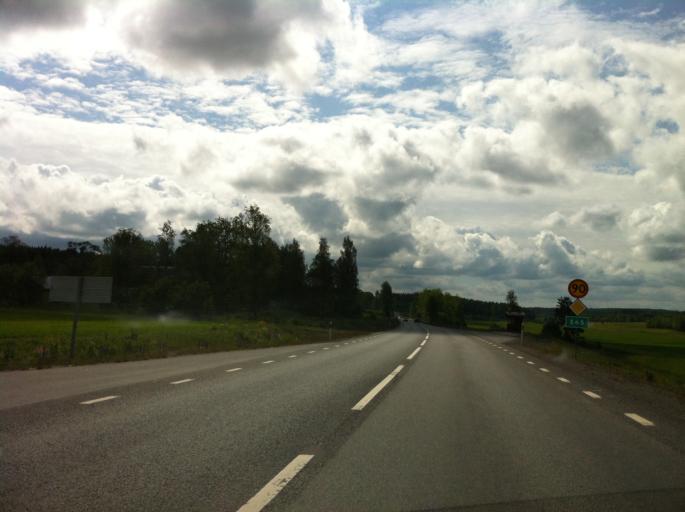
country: SE
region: Vaermland
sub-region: Karlstads Kommun
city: Edsvalla
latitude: 59.5597
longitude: 13.1870
